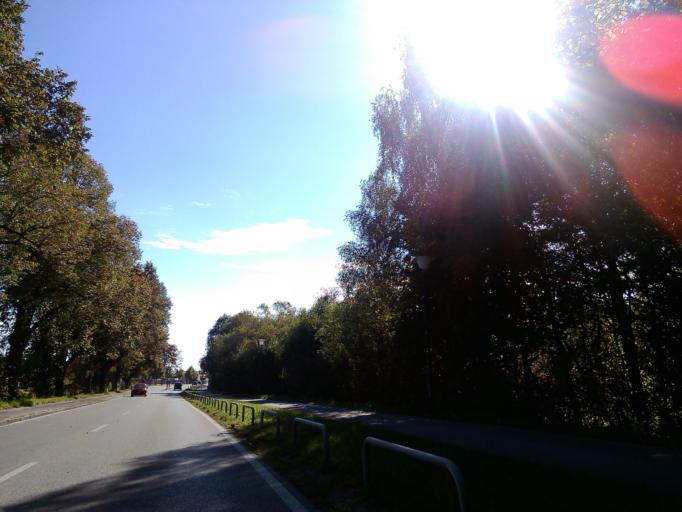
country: DE
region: Bavaria
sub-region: Upper Bavaria
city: Starnberg
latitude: 48.0152
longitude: 11.3493
